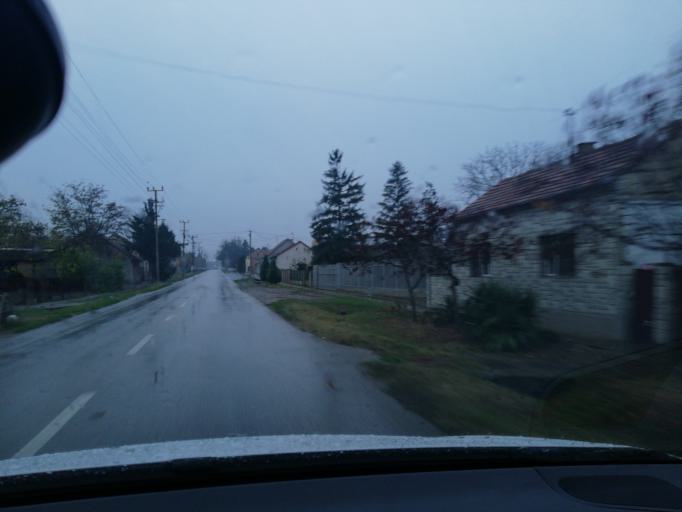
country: RS
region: Autonomna Pokrajina Vojvodina
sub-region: Sremski Okrug
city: Ruma
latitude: 45.0035
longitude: 19.8414
